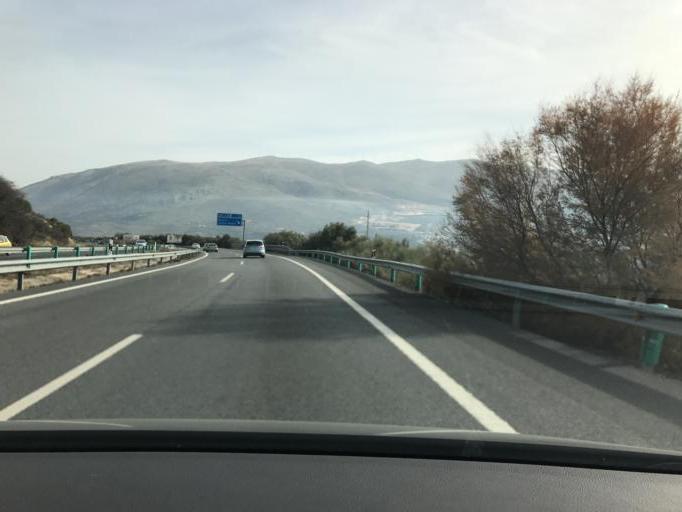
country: ES
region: Andalusia
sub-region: Provincia de Granada
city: Loja
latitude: 37.1455
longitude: -4.2392
